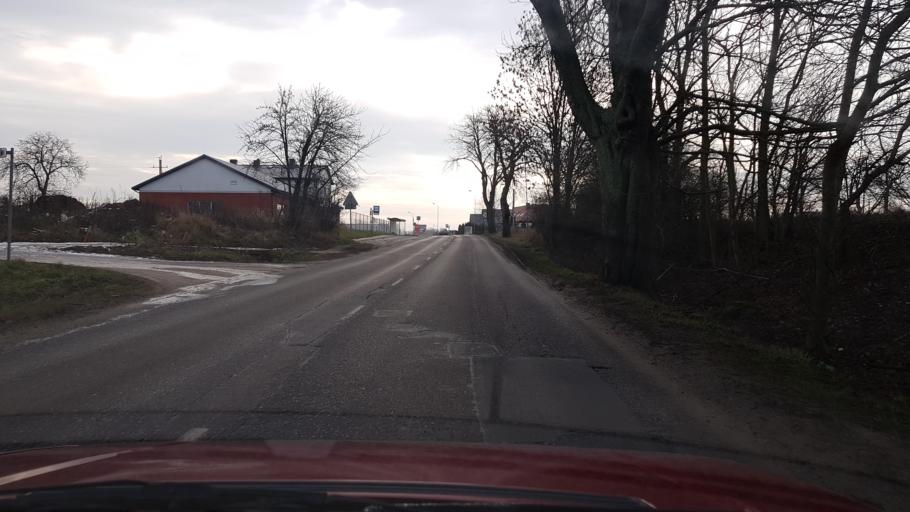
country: PL
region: West Pomeranian Voivodeship
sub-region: Powiat policki
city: Police
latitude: 53.5106
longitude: 14.5693
